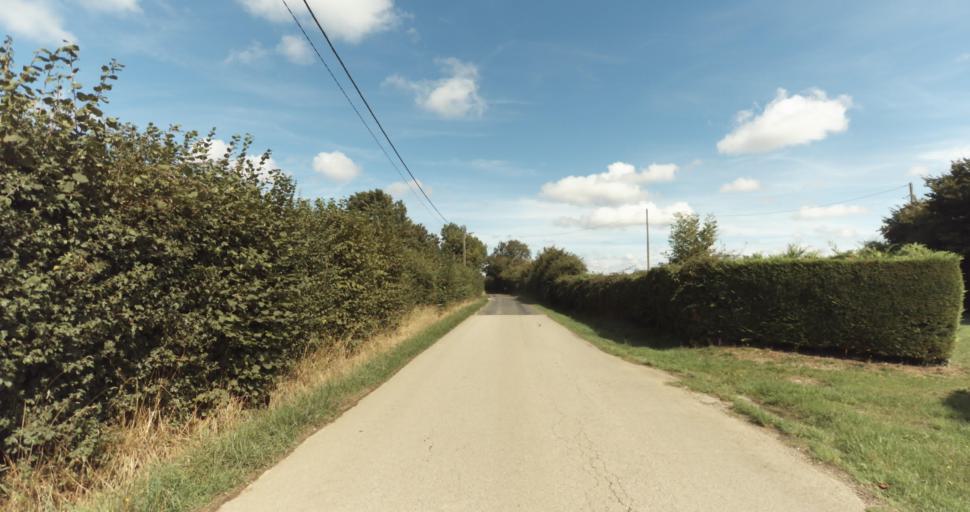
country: FR
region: Lower Normandy
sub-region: Departement du Calvados
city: Orbec
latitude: 48.9266
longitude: 0.3795
